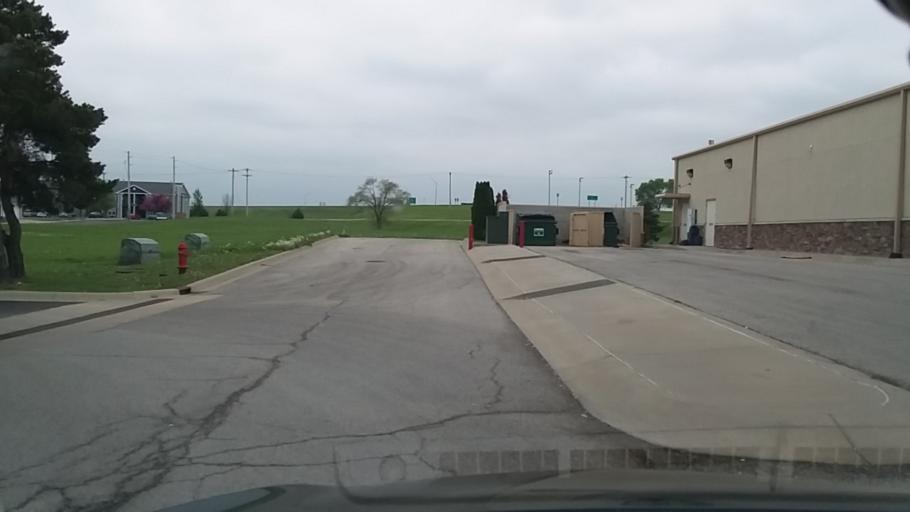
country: US
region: Kansas
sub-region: Douglas County
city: Eudora
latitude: 38.9331
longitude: -95.0951
